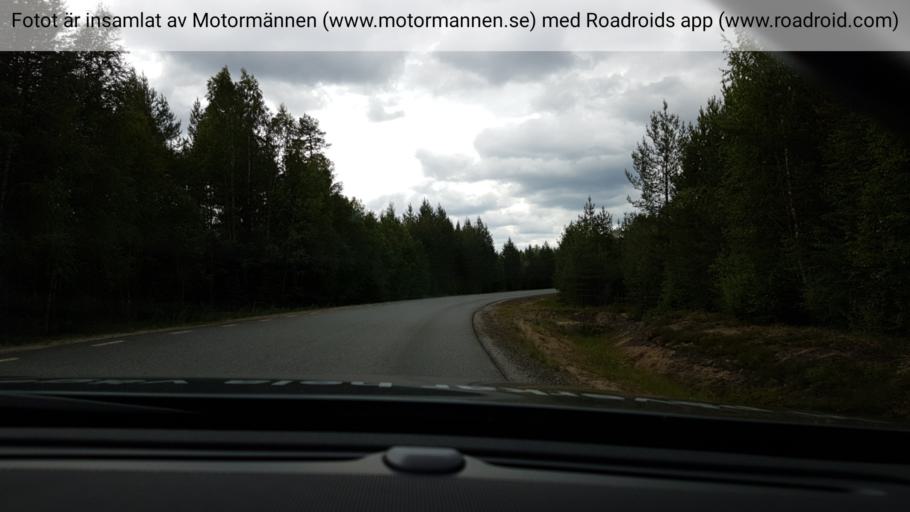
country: SE
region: Vaesterbotten
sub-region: Vindelns Kommun
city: Vindeln
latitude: 64.1801
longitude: 19.6758
